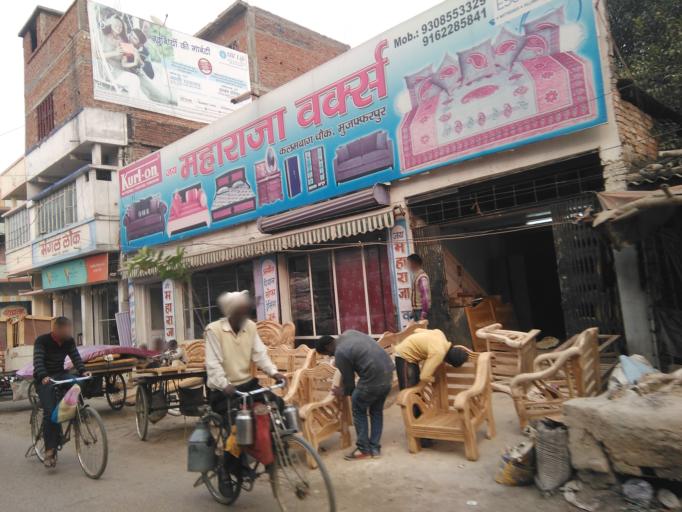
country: IN
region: Bihar
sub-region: Muzaffarpur
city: Muzaffarpur
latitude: 26.1128
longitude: 85.3840
